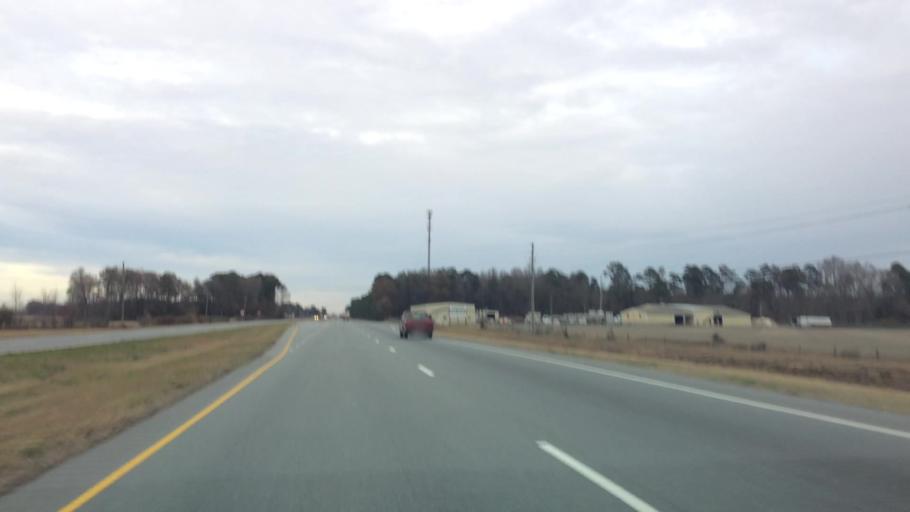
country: US
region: North Carolina
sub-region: Wayne County
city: Mount Olive
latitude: 35.1616
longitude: -78.1080
